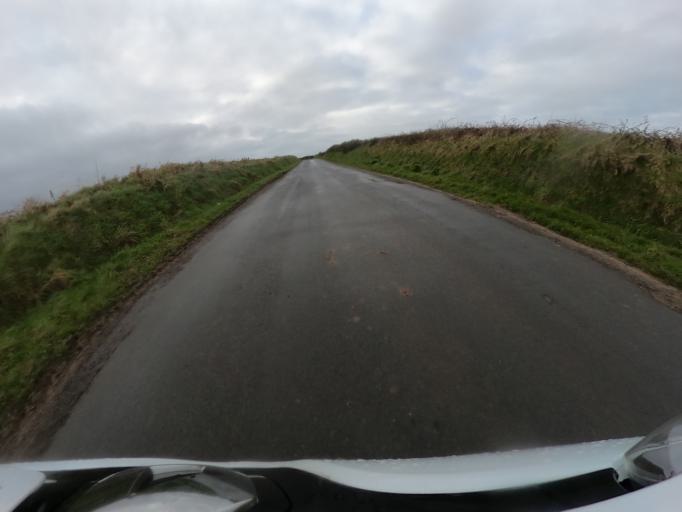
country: IM
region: Ramsey
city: Ramsey
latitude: 54.3631
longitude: -4.4574
